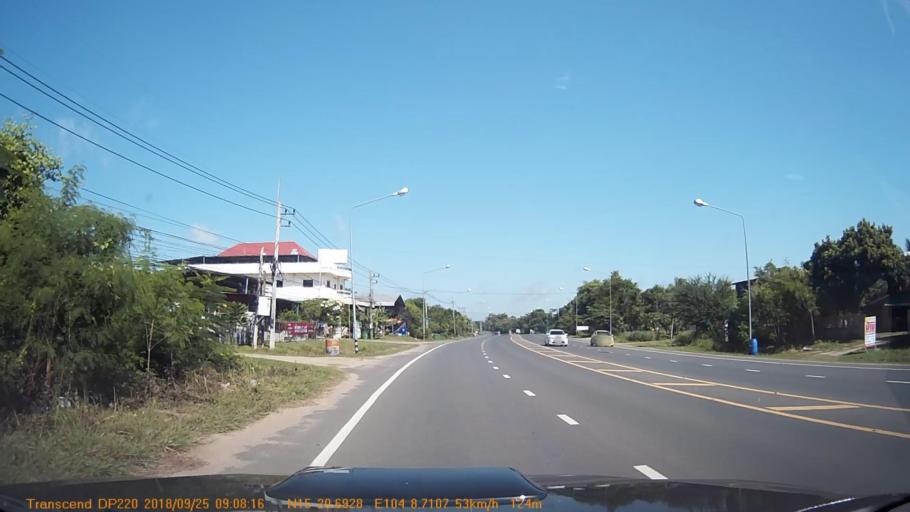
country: TH
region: Sisaket
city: Rasi Salai
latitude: 15.3448
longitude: 104.1452
